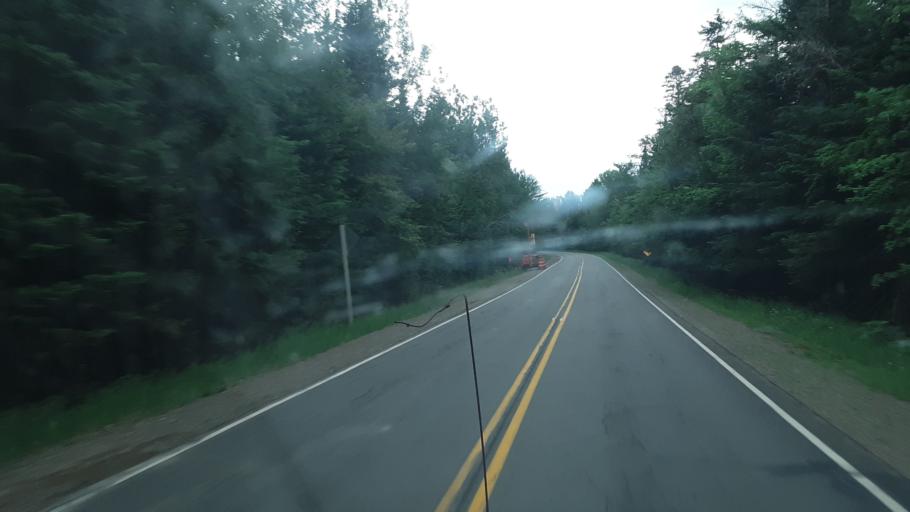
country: US
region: Maine
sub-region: Penobscot County
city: Medway
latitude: 45.7063
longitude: -68.2921
